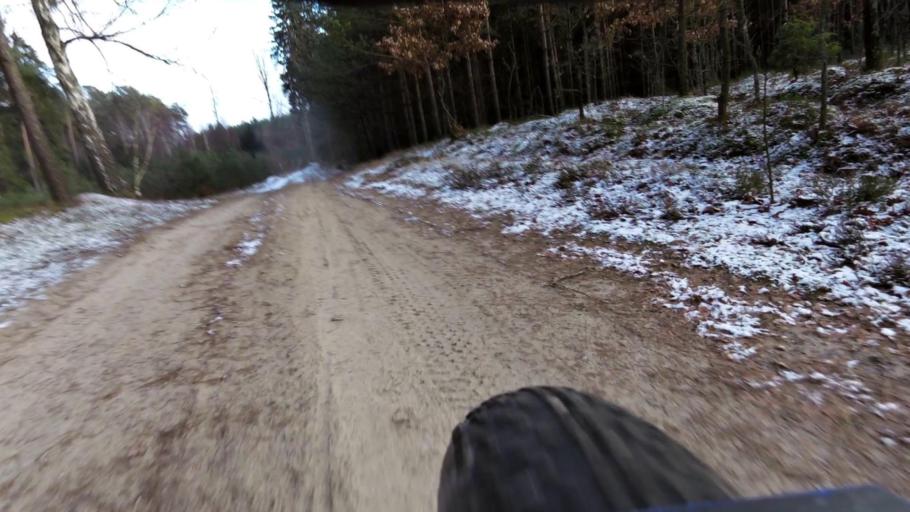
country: PL
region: West Pomeranian Voivodeship
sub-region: Powiat walecki
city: Walcz
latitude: 53.2526
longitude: 16.3659
